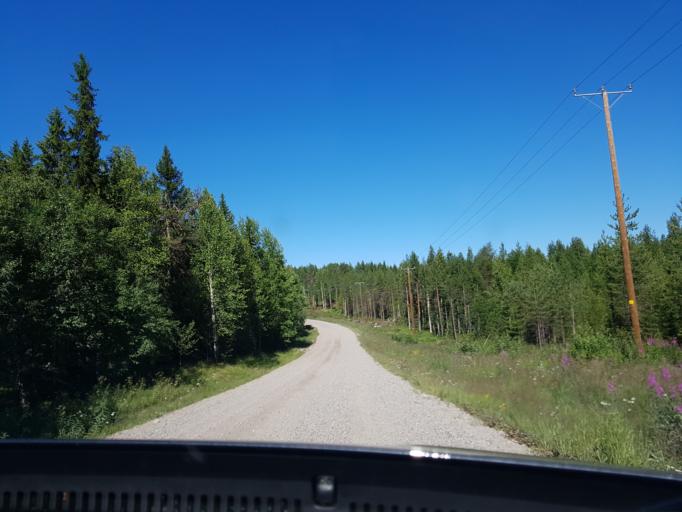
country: FI
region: Kainuu
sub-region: Kehys-Kainuu
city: Kuhmo
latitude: 64.1743
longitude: 29.6344
